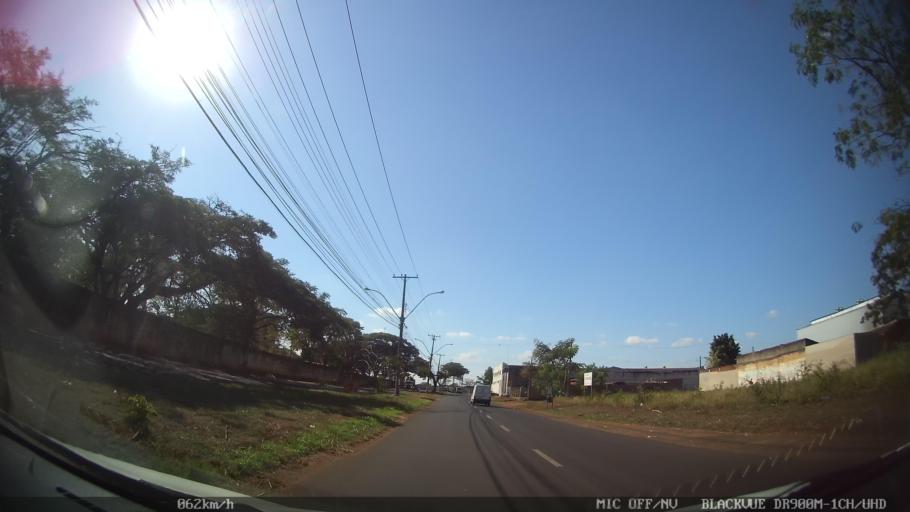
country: BR
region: Sao Paulo
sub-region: Ribeirao Preto
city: Ribeirao Preto
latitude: -21.1524
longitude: -47.7676
